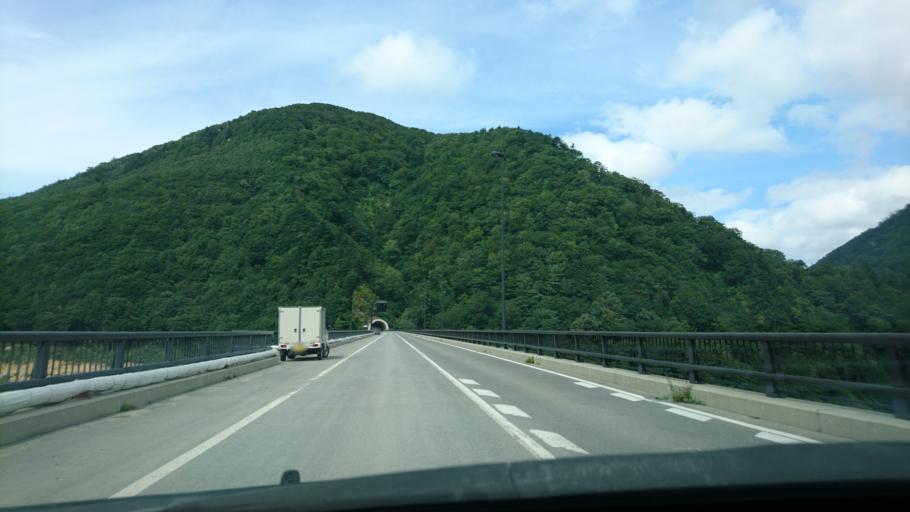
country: JP
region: Akita
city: Yuzawa
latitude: 39.0365
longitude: 140.7351
